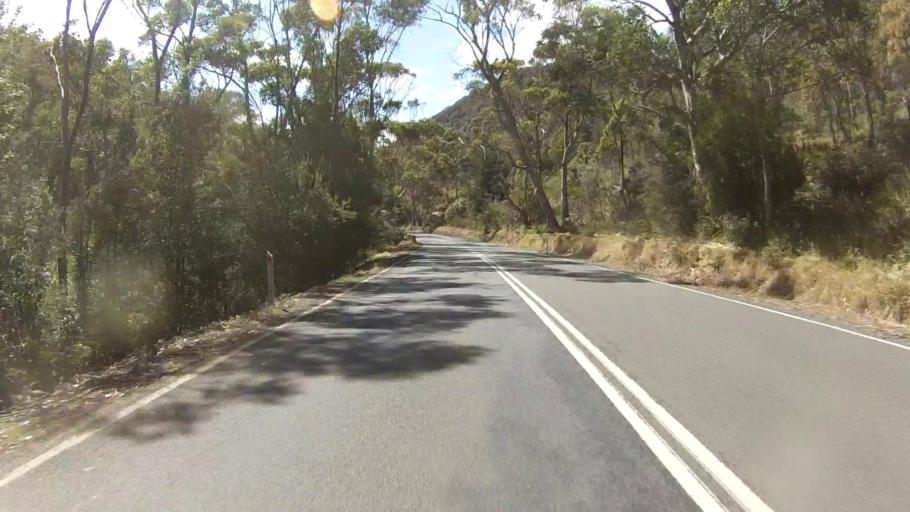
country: AU
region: Tasmania
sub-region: Derwent Valley
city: New Norfolk
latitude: -42.6799
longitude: 146.7514
